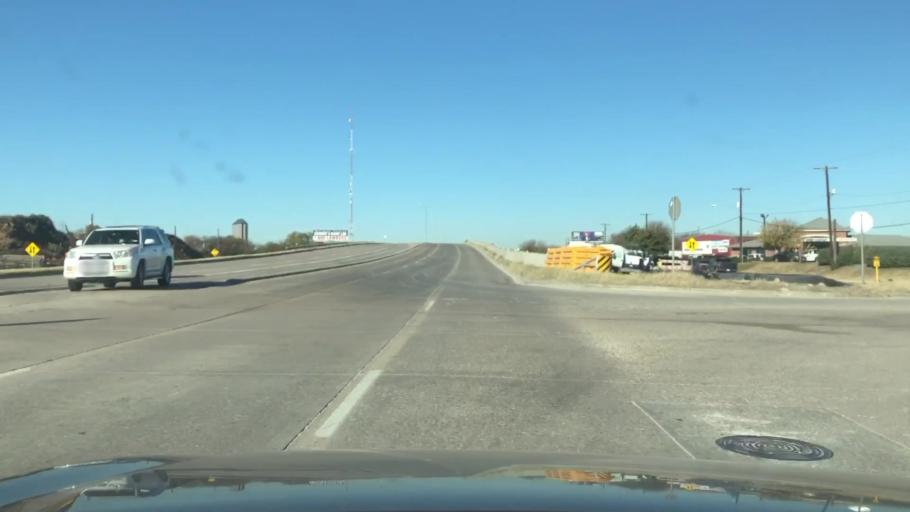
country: US
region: Texas
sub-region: Dallas County
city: Farmers Branch
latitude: 32.8689
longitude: -96.9129
